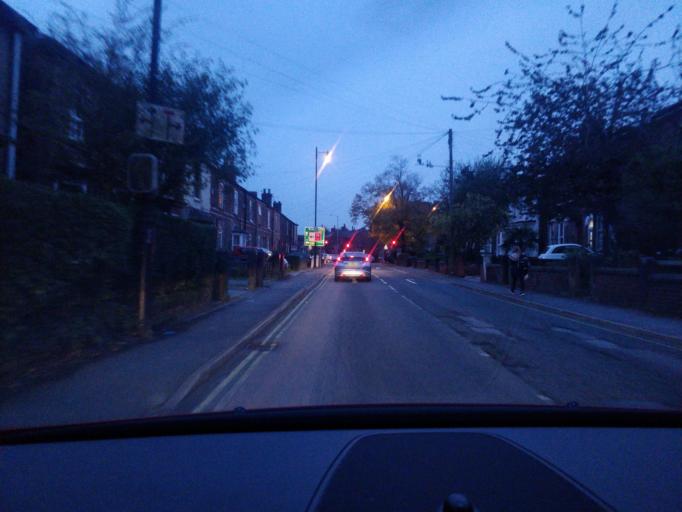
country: GB
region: England
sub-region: Lancashire
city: Ormskirk
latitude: 53.5676
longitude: -2.8813
